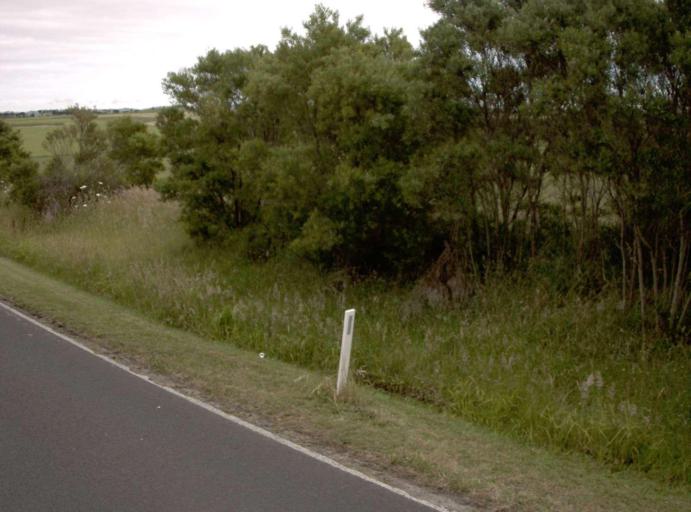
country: AU
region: Victoria
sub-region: Bass Coast
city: North Wonthaggi
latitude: -38.5556
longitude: 145.6501
